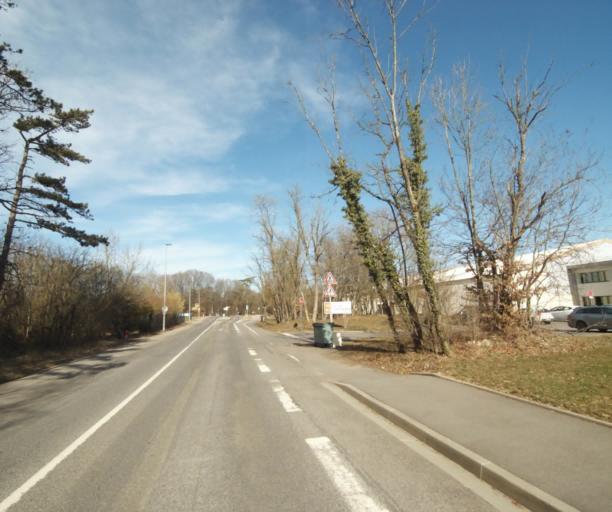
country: FR
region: Lorraine
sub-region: Departement de Meurthe-et-Moselle
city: Villers-les-Nancy
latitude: 48.6596
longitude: 6.1286
